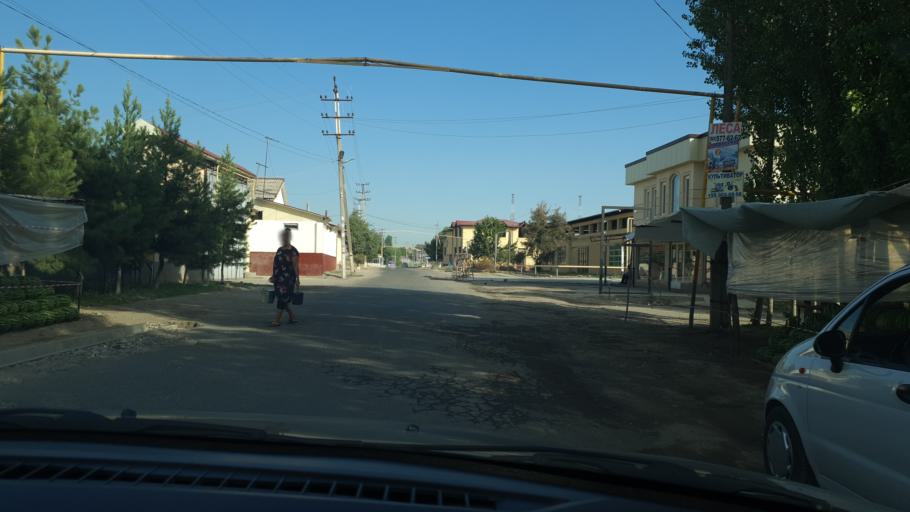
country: UZ
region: Toshkent
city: Urtaowul
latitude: 41.2028
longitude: 69.1533
